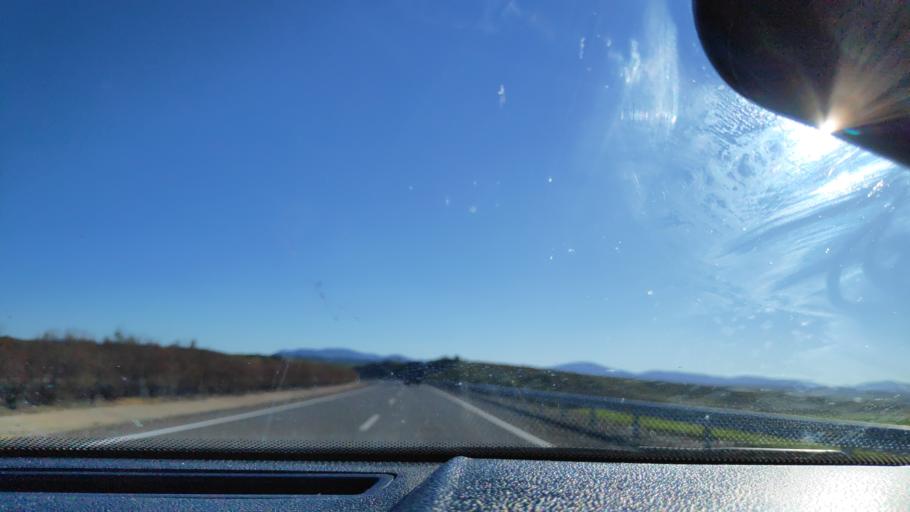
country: ES
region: Extremadura
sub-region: Provincia de Badajoz
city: Fuente de Cantos
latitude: 38.1826
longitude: -6.2797
